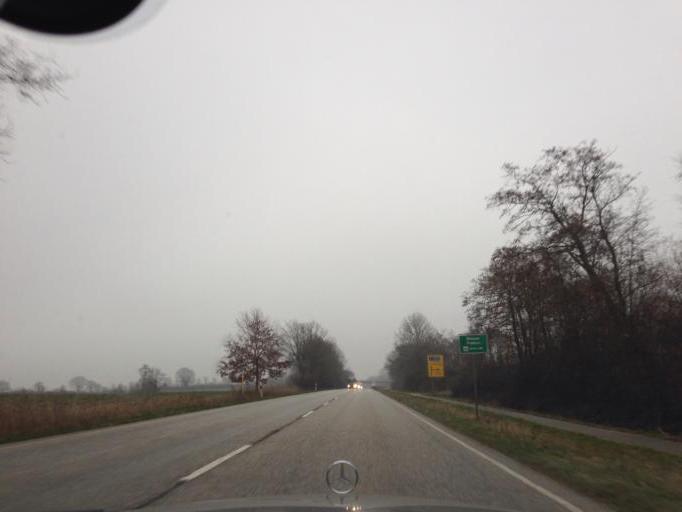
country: DE
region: Schleswig-Holstein
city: Kirchbarkau
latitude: 54.2289
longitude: 10.1463
